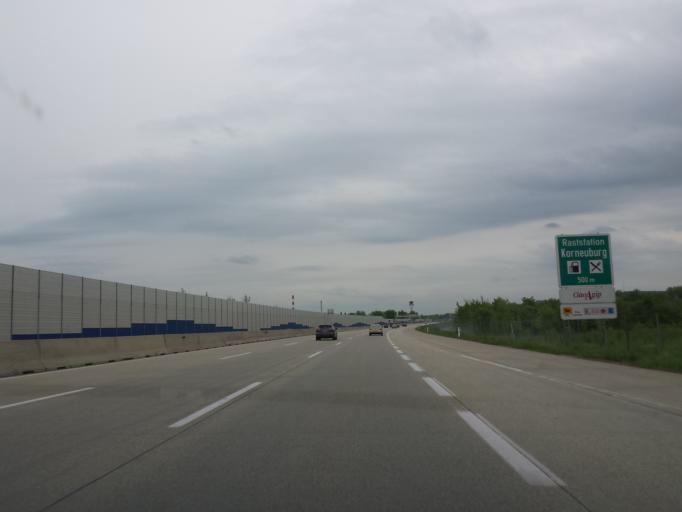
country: AT
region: Lower Austria
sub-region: Politischer Bezirk Korneuburg
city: Korneuburg
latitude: 48.3532
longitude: 16.3157
